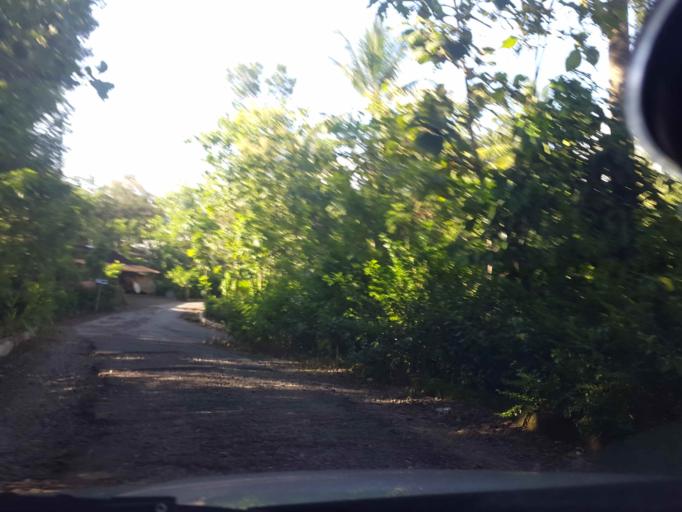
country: ID
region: Central Java
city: Jatiroto
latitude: -7.8109
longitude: 111.0990
